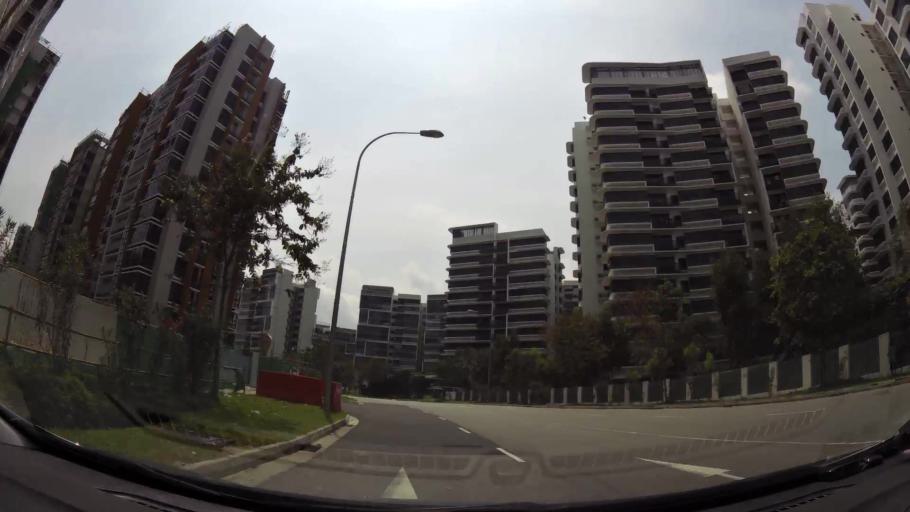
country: MY
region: Johor
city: Kampung Pasir Gudang Baru
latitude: 1.3720
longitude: 103.9448
